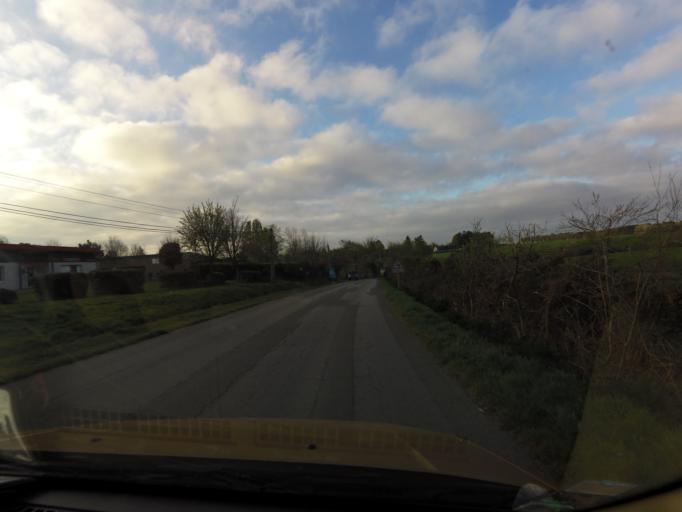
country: FR
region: Brittany
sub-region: Departement du Morbihan
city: Arradon
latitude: 47.6443
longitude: -2.8084
